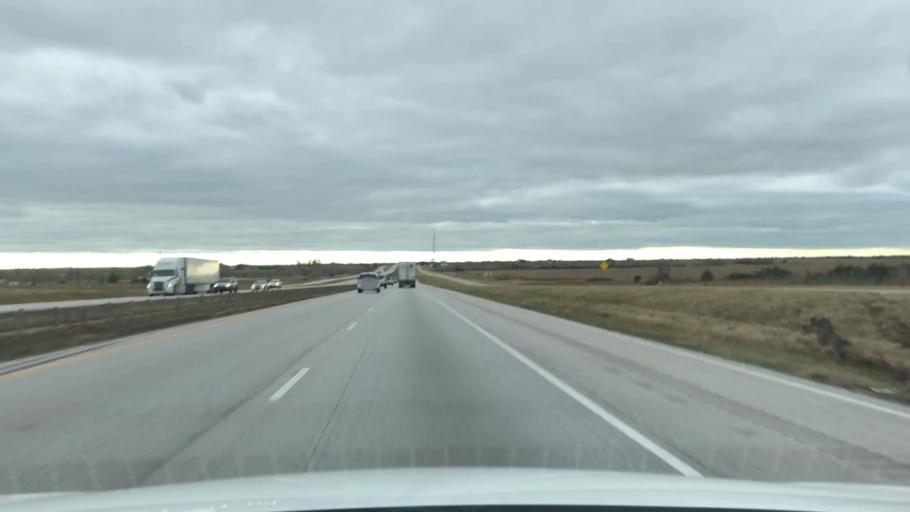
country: US
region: Texas
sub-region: Colorado County
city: Eagle Lake
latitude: 29.7385
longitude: -96.3504
